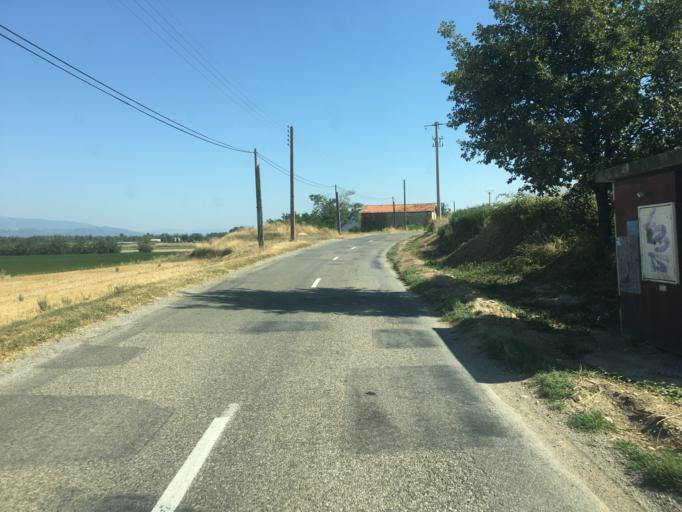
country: FR
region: Provence-Alpes-Cote d'Azur
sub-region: Departement des Alpes-de-Haute-Provence
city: Villeneuve
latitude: 43.8636
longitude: 5.8941
